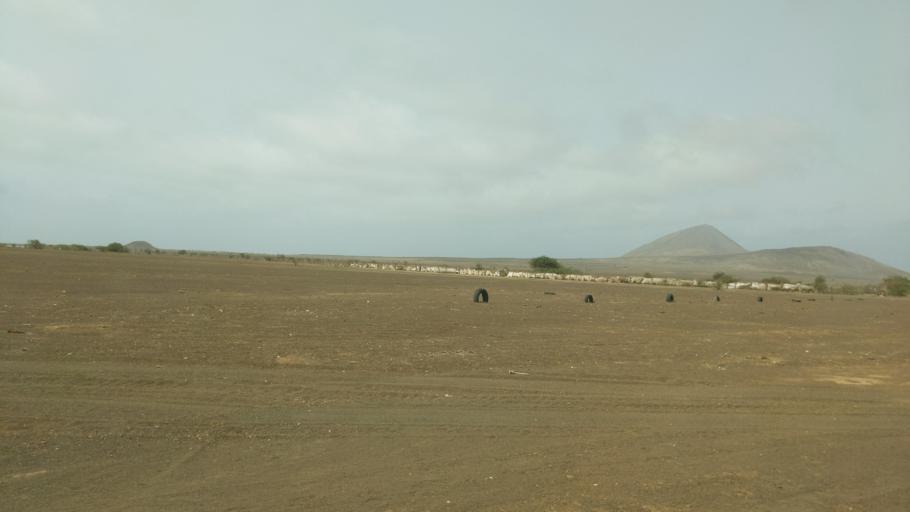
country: CV
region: Sal
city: Espargos
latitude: 16.7970
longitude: -22.9551
